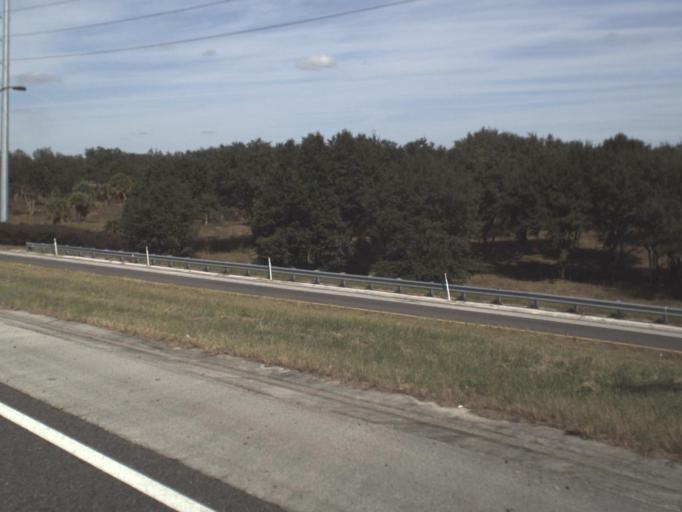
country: US
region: Florida
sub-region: Polk County
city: Loughman
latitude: 28.2852
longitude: -81.5947
